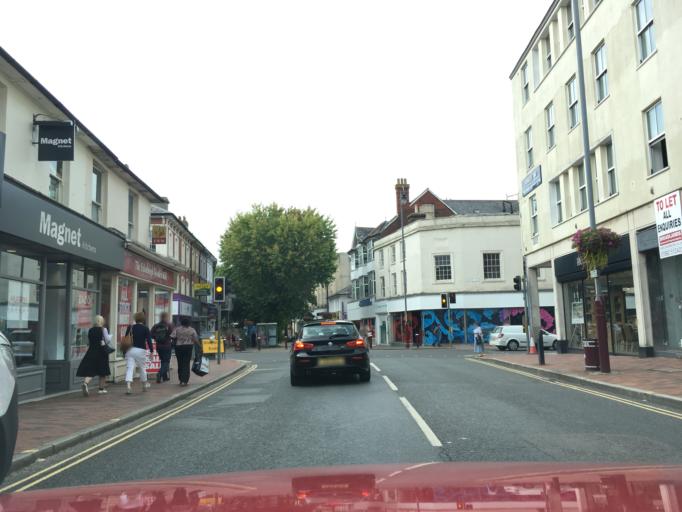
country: GB
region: England
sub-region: Kent
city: Royal Tunbridge Wells
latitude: 51.1337
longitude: 0.2668
